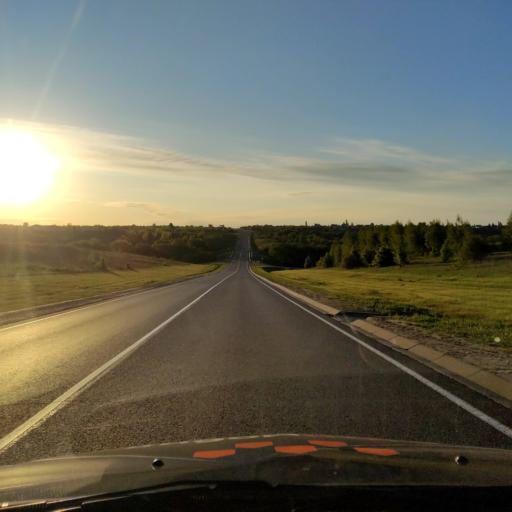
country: RU
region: Orjol
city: Livny
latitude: 52.4494
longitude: 37.6088
